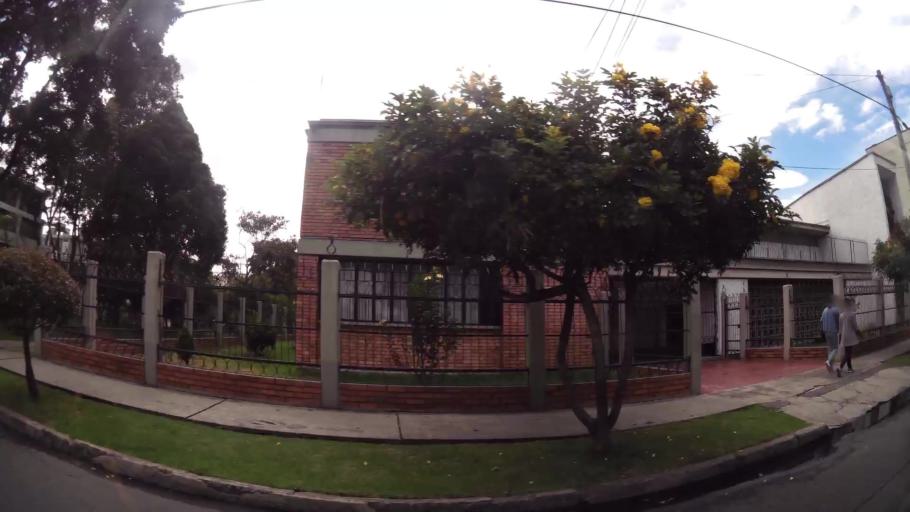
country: CO
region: Bogota D.C.
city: Barrio San Luis
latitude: 4.6826
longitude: -74.0616
